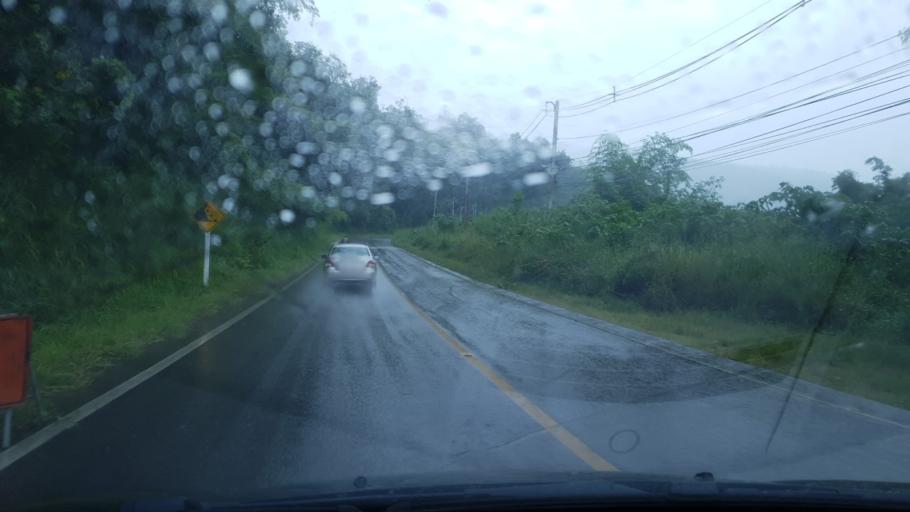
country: TH
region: Mae Hong Son
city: Khun Yuam
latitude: 18.6609
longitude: 97.9300
